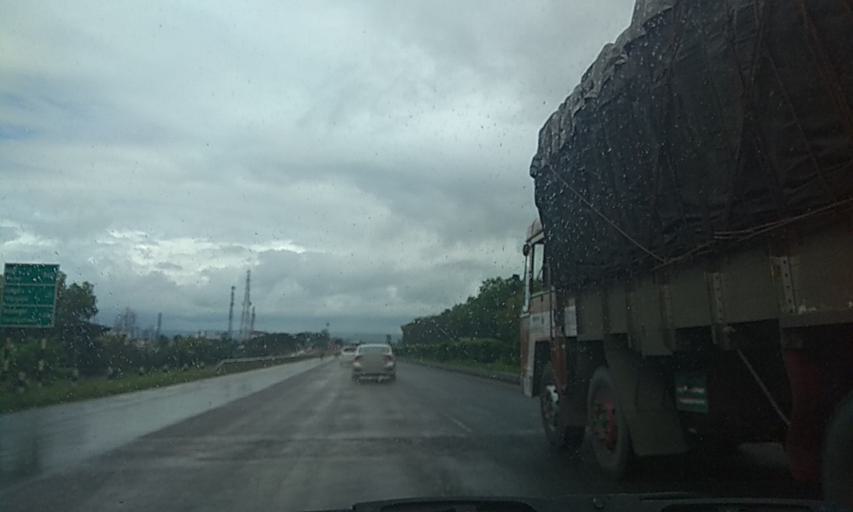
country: IN
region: Karnataka
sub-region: Belgaum
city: Belgaum
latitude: 15.8923
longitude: 74.5238
